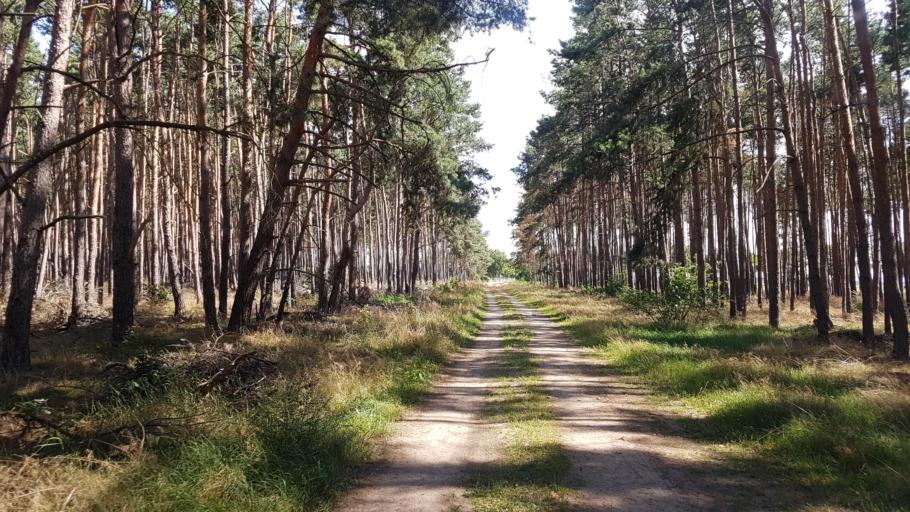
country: DE
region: Brandenburg
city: Muhlberg
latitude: 51.4684
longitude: 13.3098
